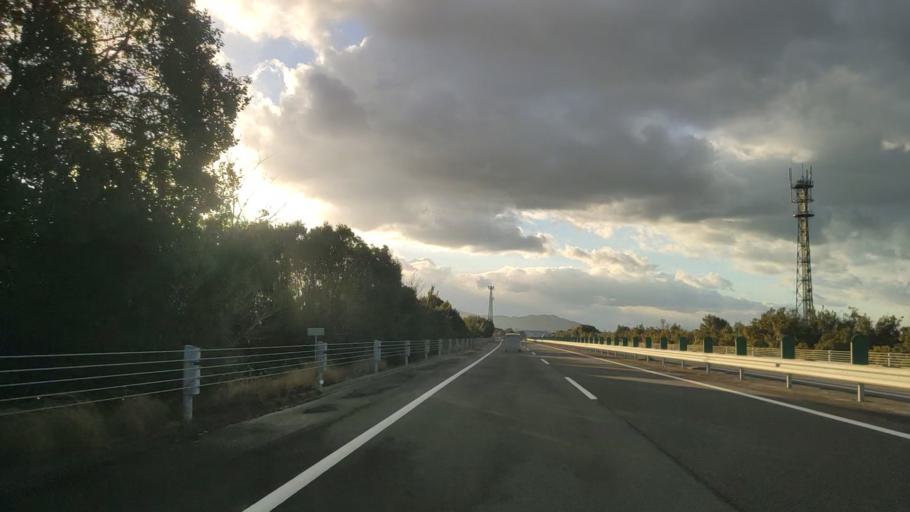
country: JP
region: Ehime
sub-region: Shikoku-chuo Shi
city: Matsuyama
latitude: 33.7853
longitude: 132.8551
